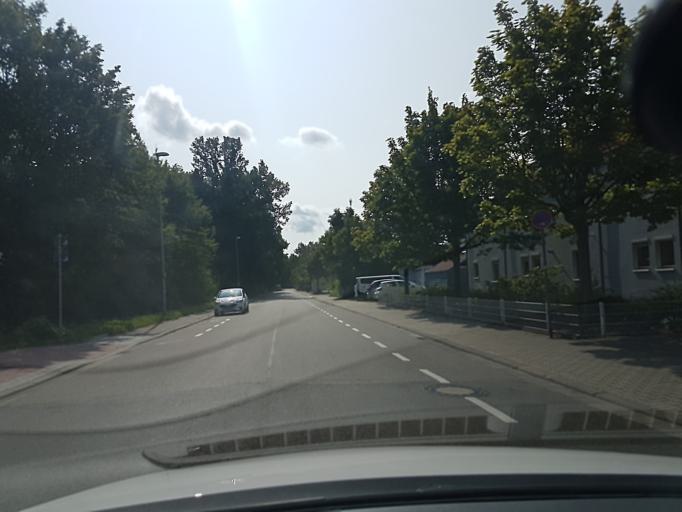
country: DE
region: Rheinland-Pfalz
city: Schifferstadt
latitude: 49.3822
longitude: 8.3926
